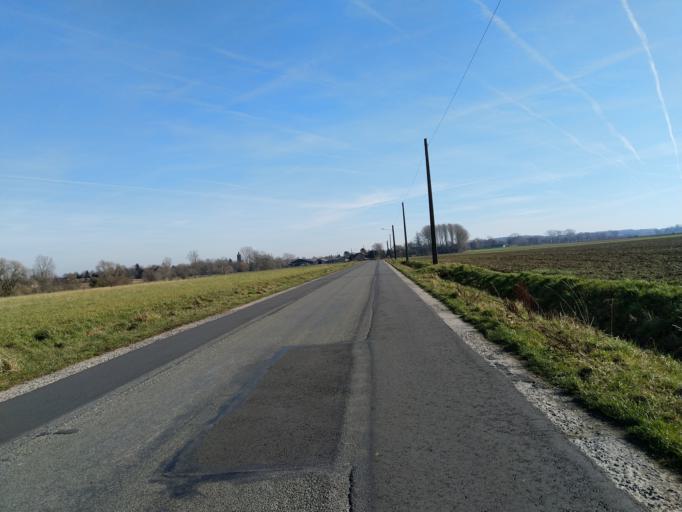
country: BE
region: Wallonia
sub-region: Province du Hainaut
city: Jurbise
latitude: 50.5303
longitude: 3.9285
